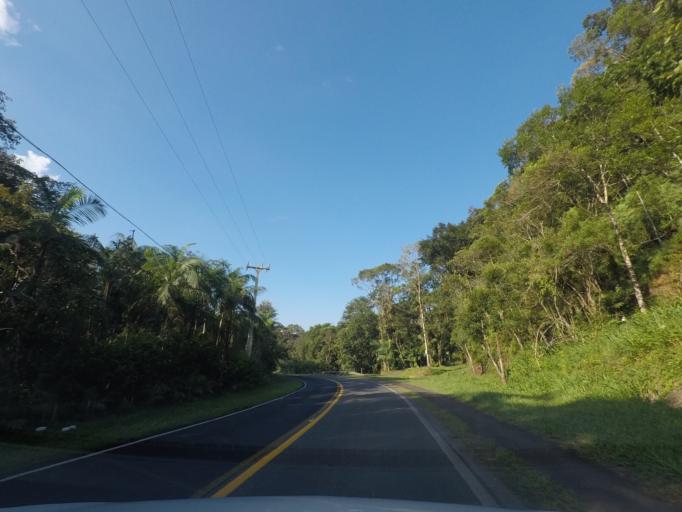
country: BR
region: Parana
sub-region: Antonina
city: Antonina
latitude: -25.3954
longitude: -48.8660
